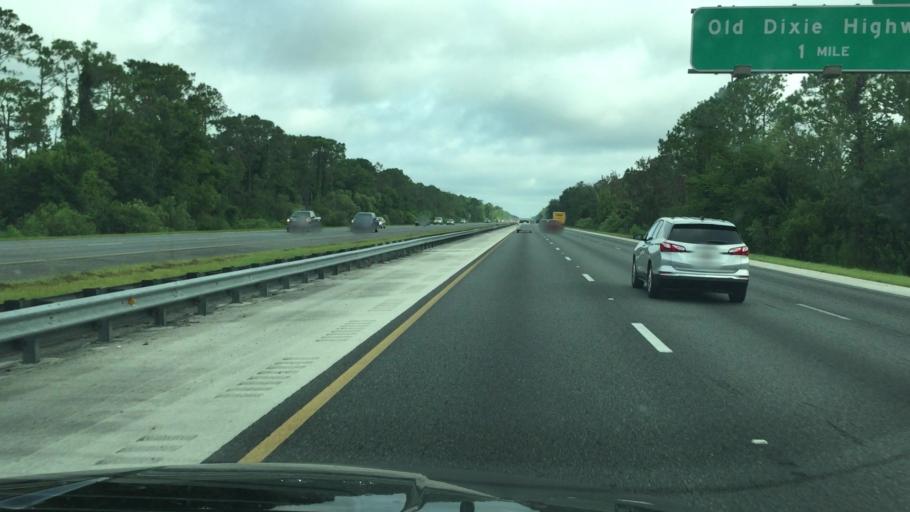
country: US
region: Florida
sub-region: Volusia County
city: Ormond-by-the-Sea
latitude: 29.3839
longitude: -81.1465
